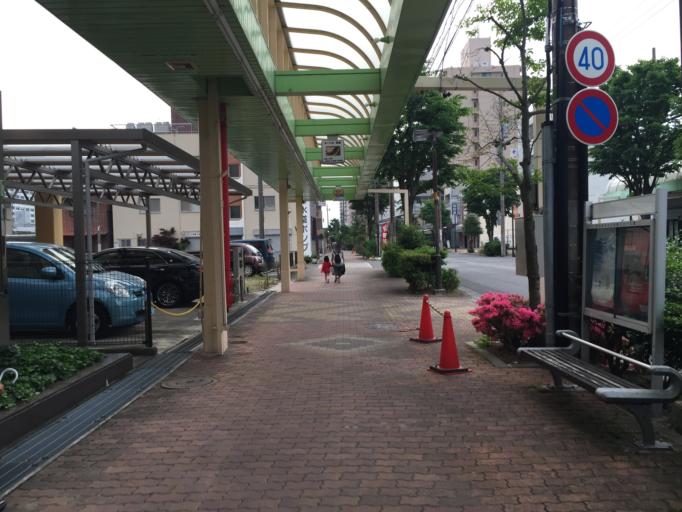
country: JP
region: Mie
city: Yokkaichi
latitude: 34.9656
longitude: 136.6291
